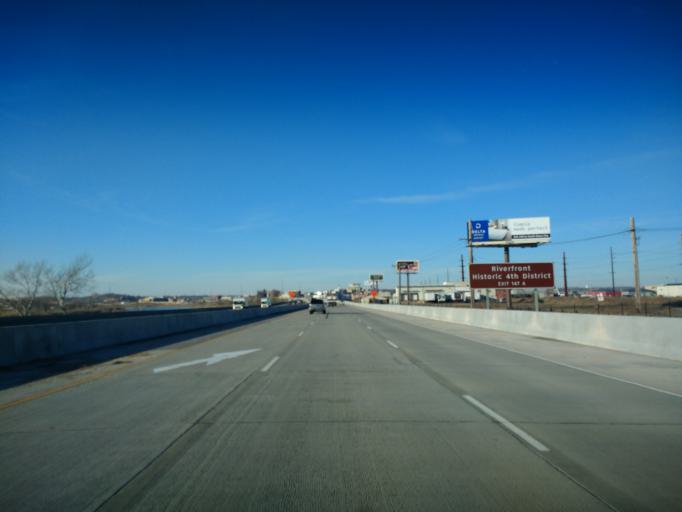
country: US
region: Iowa
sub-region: Woodbury County
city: Sioux City
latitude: 42.4774
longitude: -96.3854
